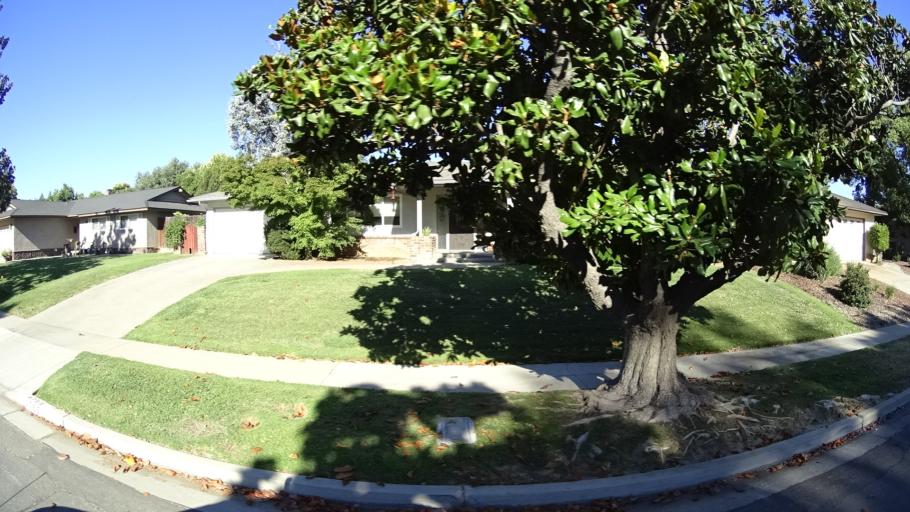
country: US
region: California
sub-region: Fresno County
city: Fresno
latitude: 36.8040
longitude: -119.8286
